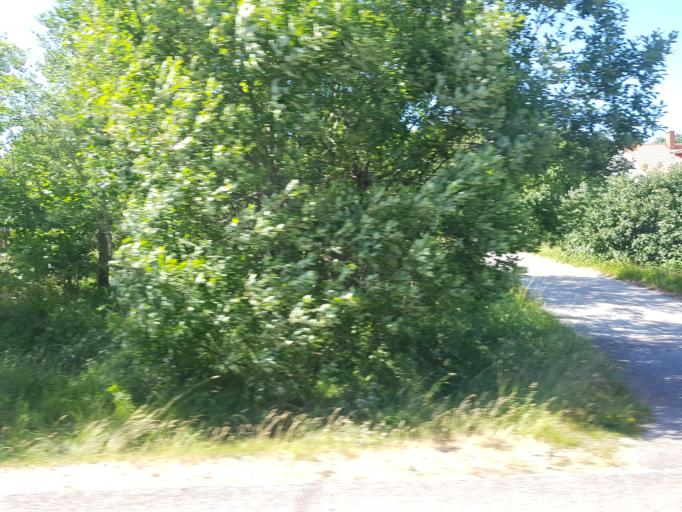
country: SE
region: Vaestra Goetaland
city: Ronnang
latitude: 57.9398
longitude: 11.5952
